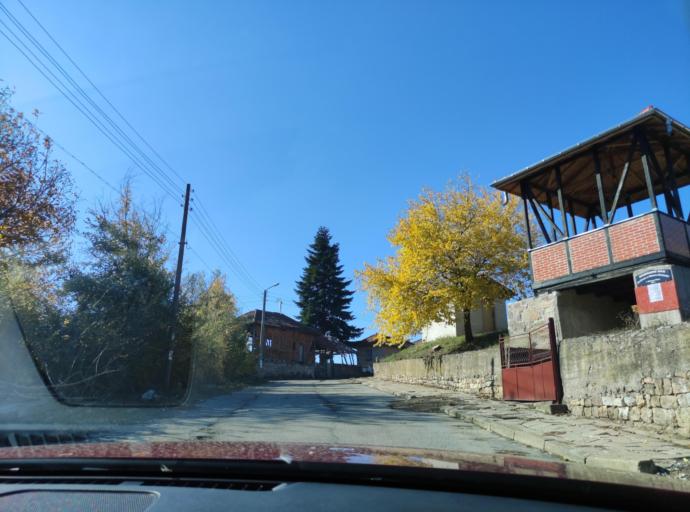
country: BG
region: Montana
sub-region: Obshtina Chiprovtsi
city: Chiprovtsi
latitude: 43.4548
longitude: 23.0329
